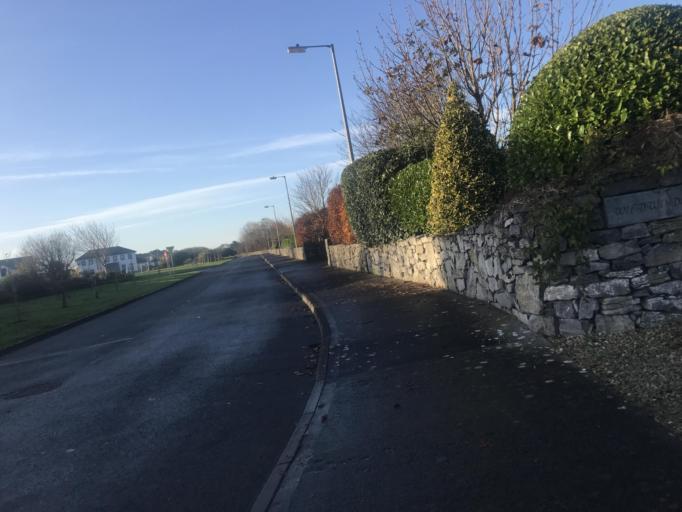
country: IE
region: Connaught
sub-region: County Galway
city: Oranmore
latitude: 53.2619
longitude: -8.9375
